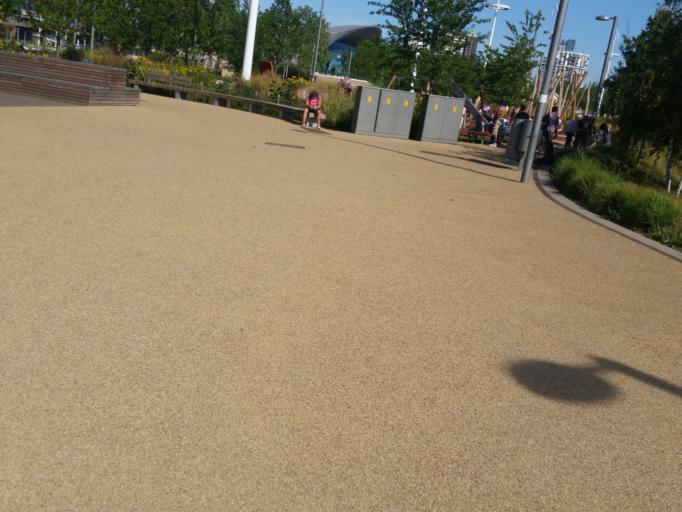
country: GB
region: England
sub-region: Greater London
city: Poplar
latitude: 51.5415
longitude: -0.0160
